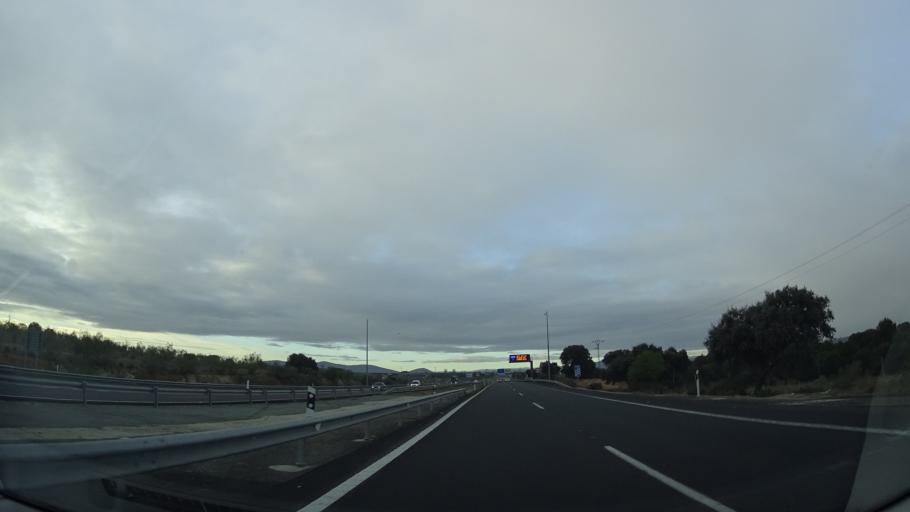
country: ES
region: Castille-La Mancha
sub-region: Province of Toledo
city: Burguillos de Toledo
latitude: 39.8293
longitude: -3.9807
